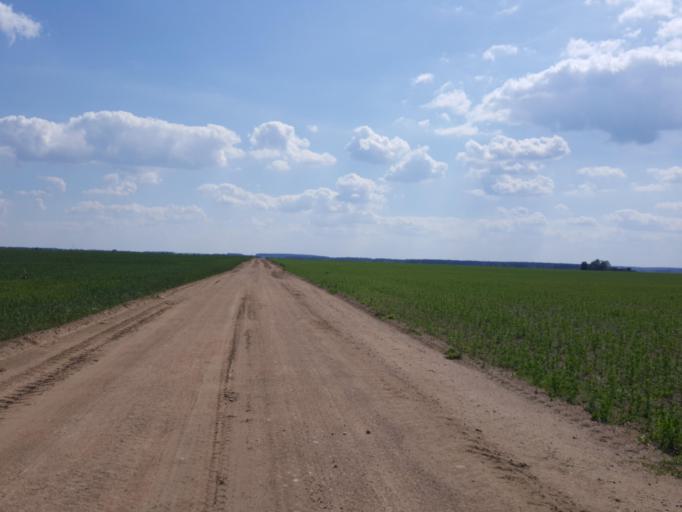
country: BY
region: Brest
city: Kamyanyuki
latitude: 52.4944
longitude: 23.6023
